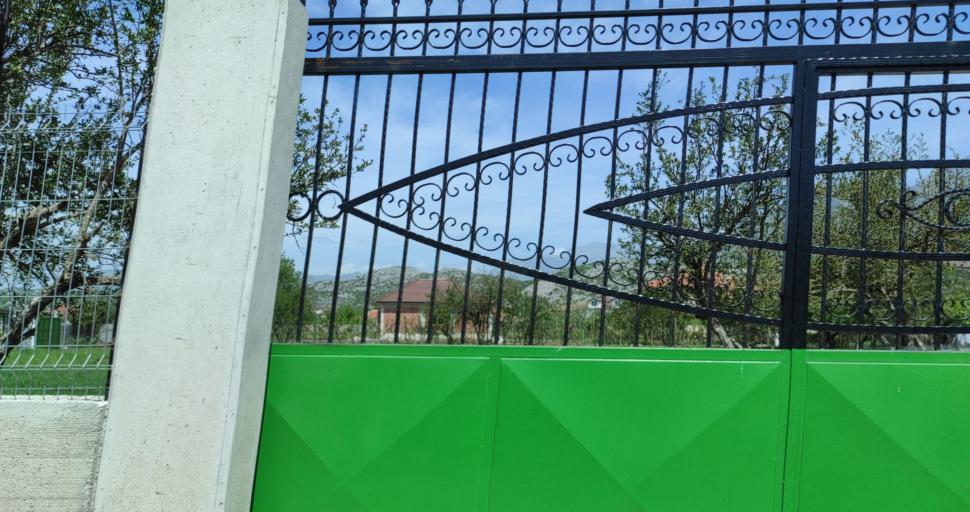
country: AL
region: Shkoder
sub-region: Rrethi i Malesia e Madhe
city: Gruemire
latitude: 42.1378
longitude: 19.5455
